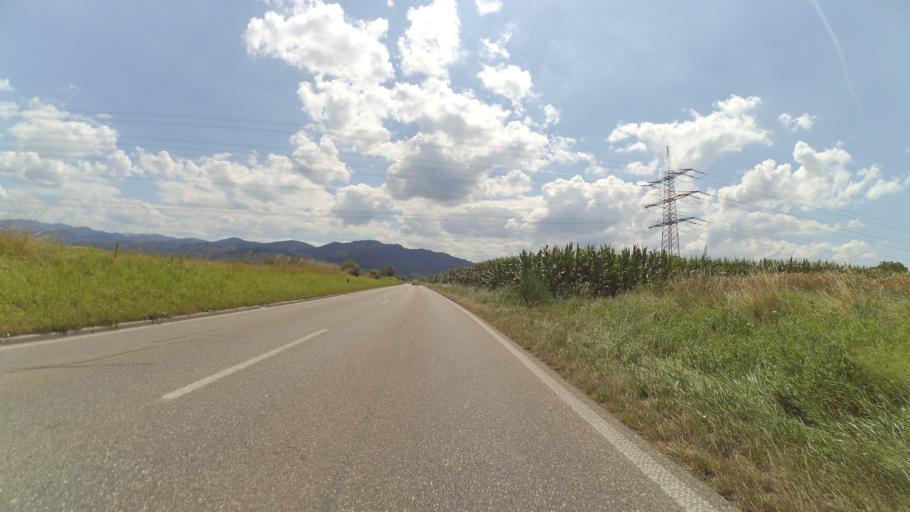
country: DE
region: Baden-Wuerttemberg
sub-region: Freiburg Region
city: Bad Krozingen
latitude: 47.9029
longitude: 7.7161
